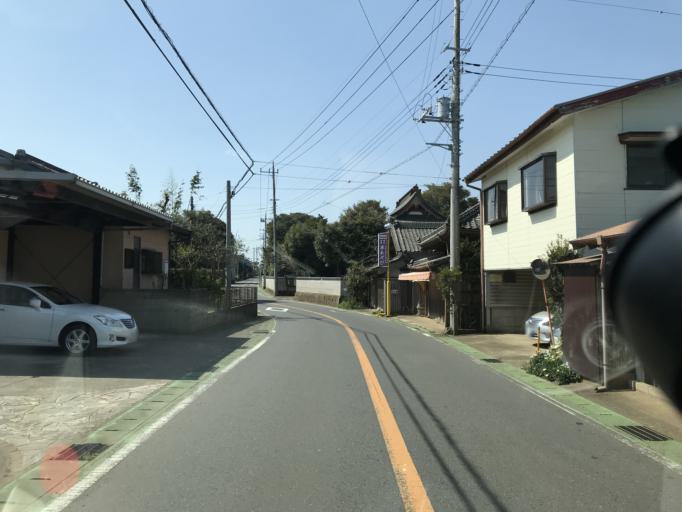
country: JP
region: Chiba
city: Asahi
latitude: 35.7920
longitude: 140.6784
